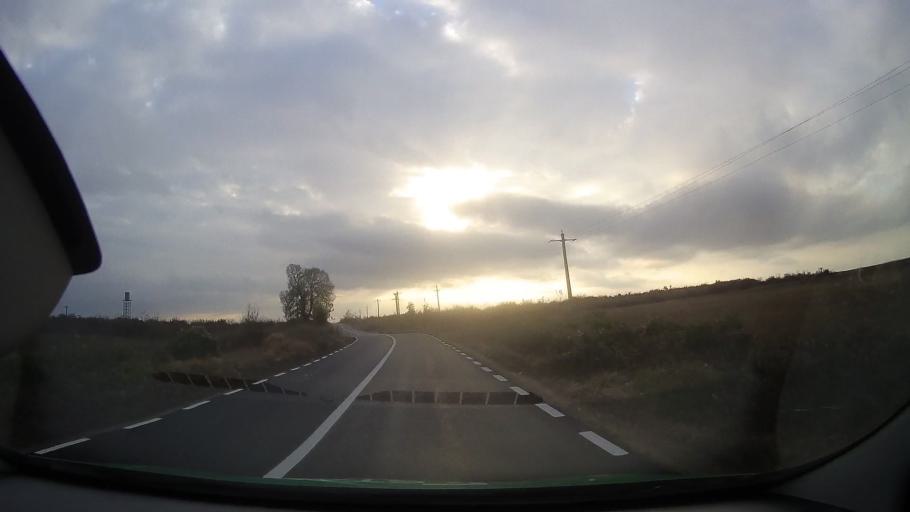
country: RO
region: Constanta
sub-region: Comuna Adamclisi
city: Adamclisi
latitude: 44.0683
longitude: 27.9773
